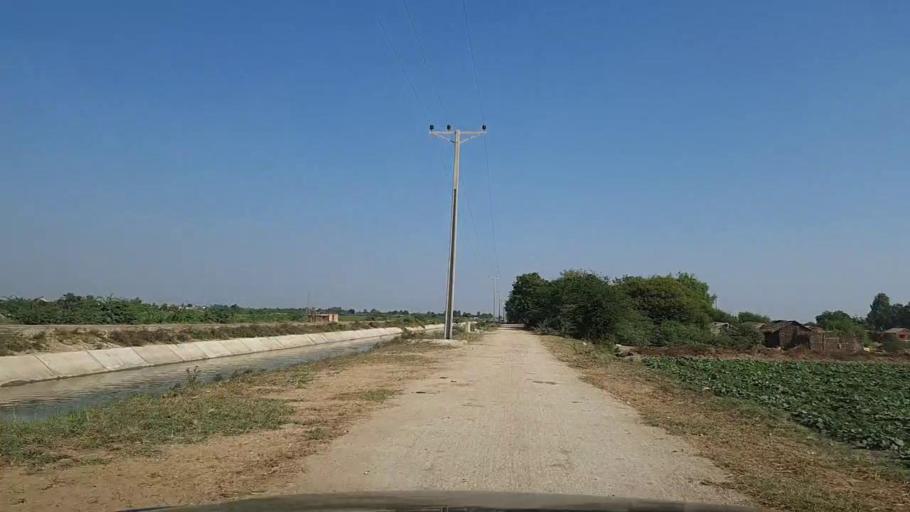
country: PK
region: Sindh
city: Mirpur Sakro
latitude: 24.5966
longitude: 67.8082
